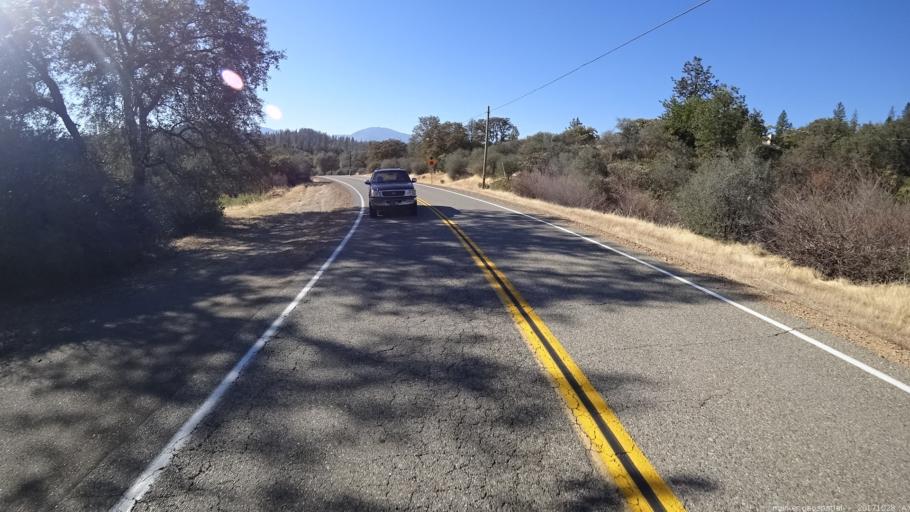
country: US
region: California
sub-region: Shasta County
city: Shasta
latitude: 40.6156
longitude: -122.4573
